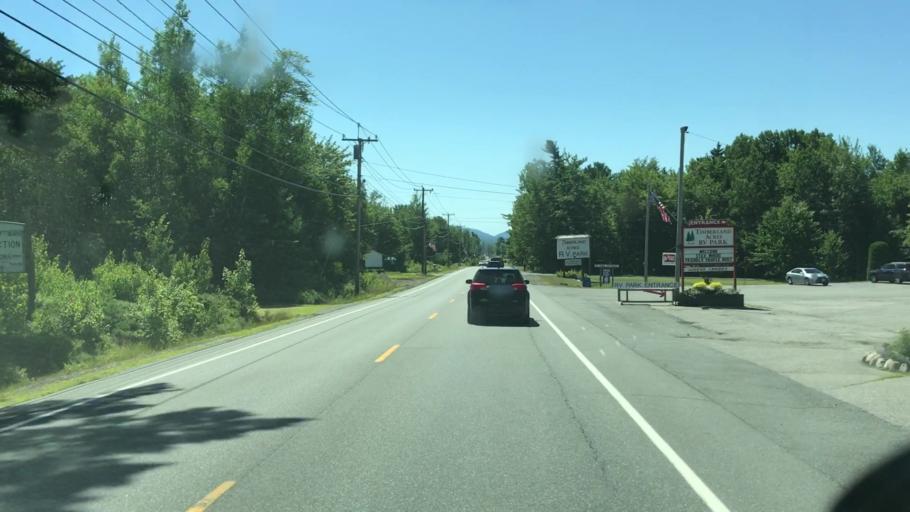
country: US
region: Maine
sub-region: Hancock County
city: Ellsworth
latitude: 44.5077
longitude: -68.3891
